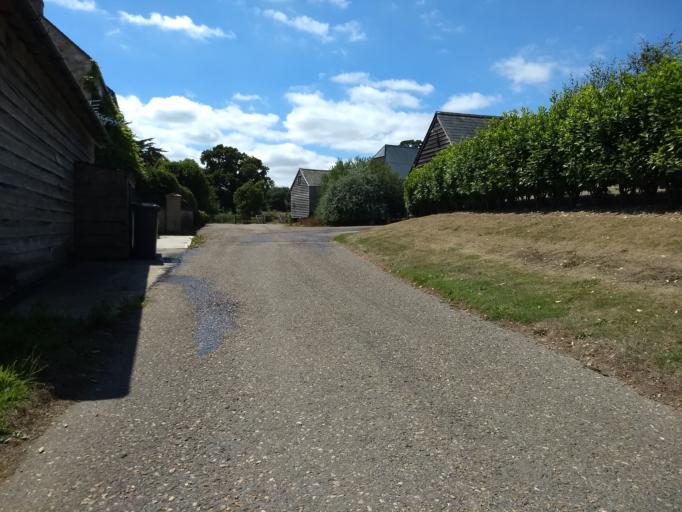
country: GB
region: England
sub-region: Isle of Wight
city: Brading
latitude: 50.7081
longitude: -1.1387
